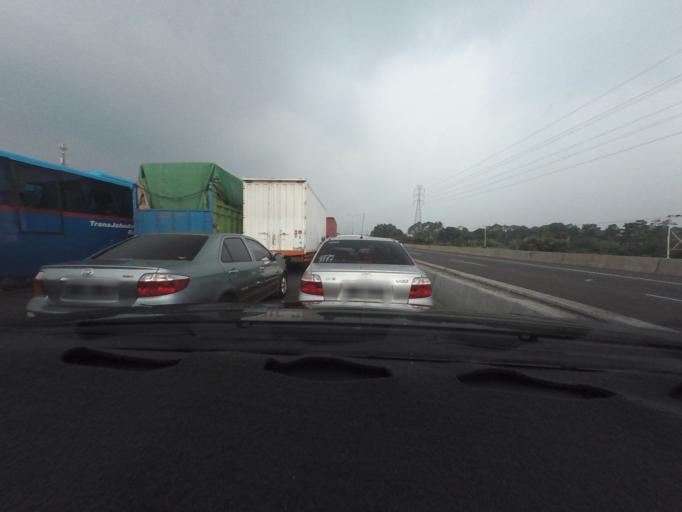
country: ID
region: West Java
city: Bogor
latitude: -6.6344
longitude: 106.8410
